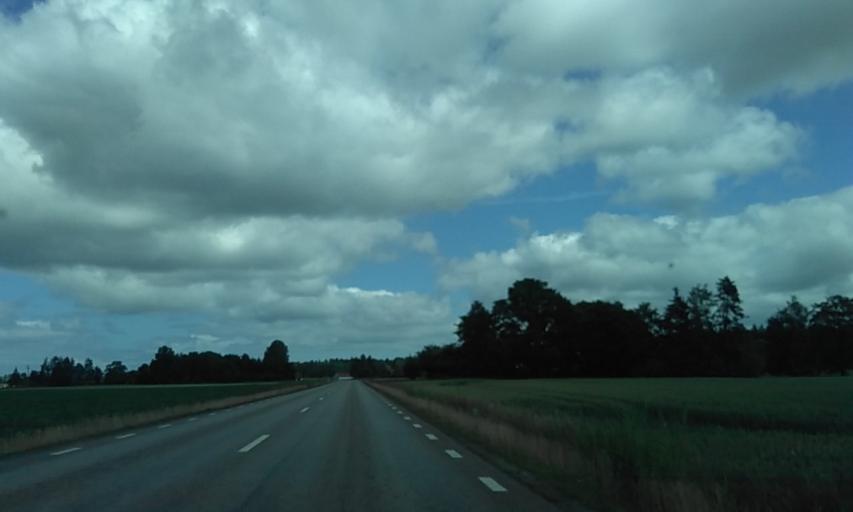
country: SE
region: Vaestra Goetaland
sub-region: Grastorps Kommun
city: Graestorp
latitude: 58.3138
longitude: 12.6715
